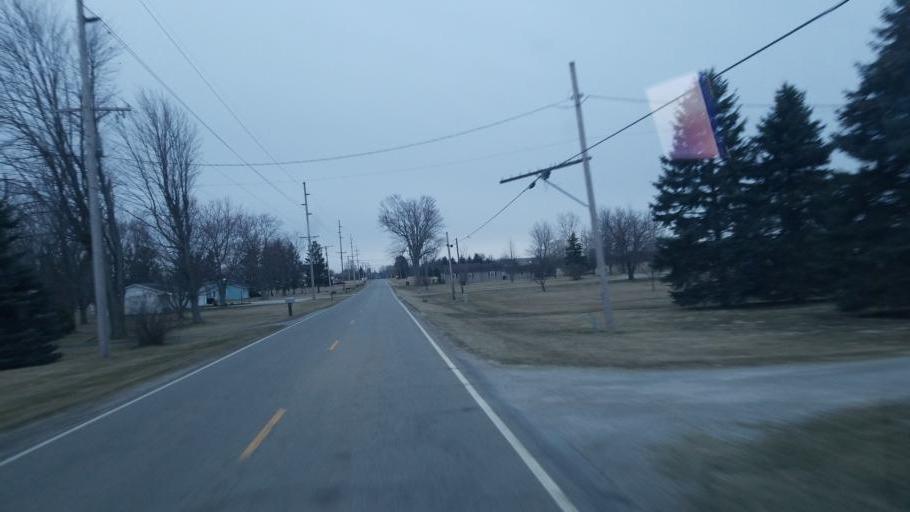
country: US
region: Ohio
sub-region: Defiance County
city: Hicksville
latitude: 41.3118
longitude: -84.7667
